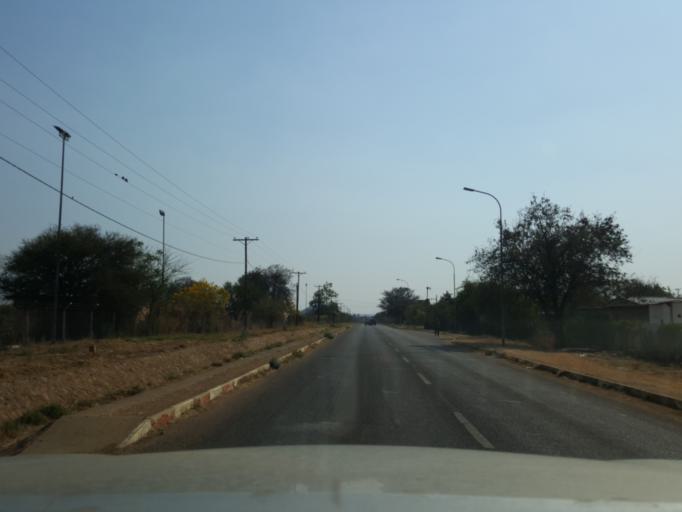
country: BW
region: South East
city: Lobatse
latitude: -25.2000
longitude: 25.6901
